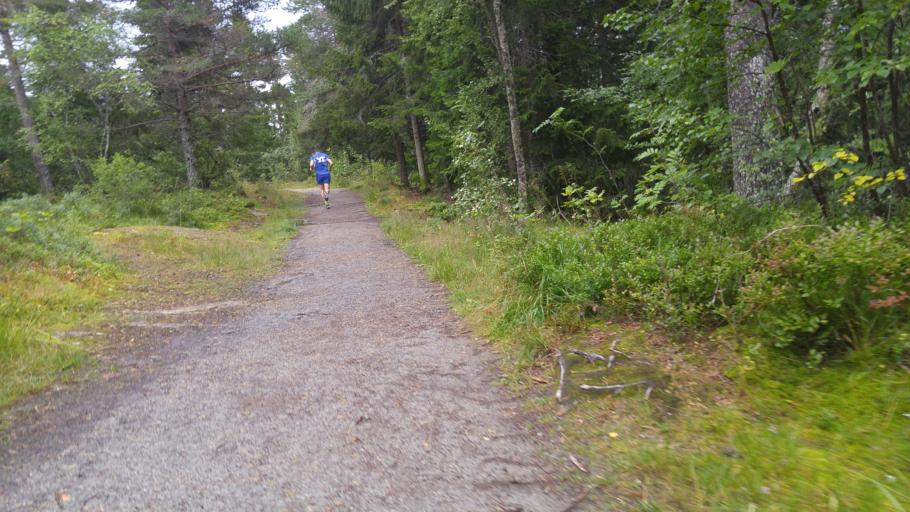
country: NO
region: Sor-Trondelag
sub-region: Trondheim
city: Trondheim
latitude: 63.4073
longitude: 10.3230
